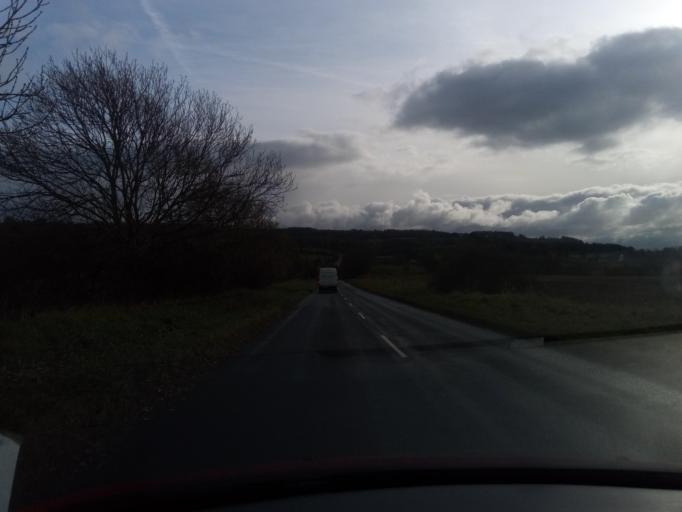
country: GB
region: England
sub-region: Northumberland
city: Wall
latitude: 55.0329
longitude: -2.1317
